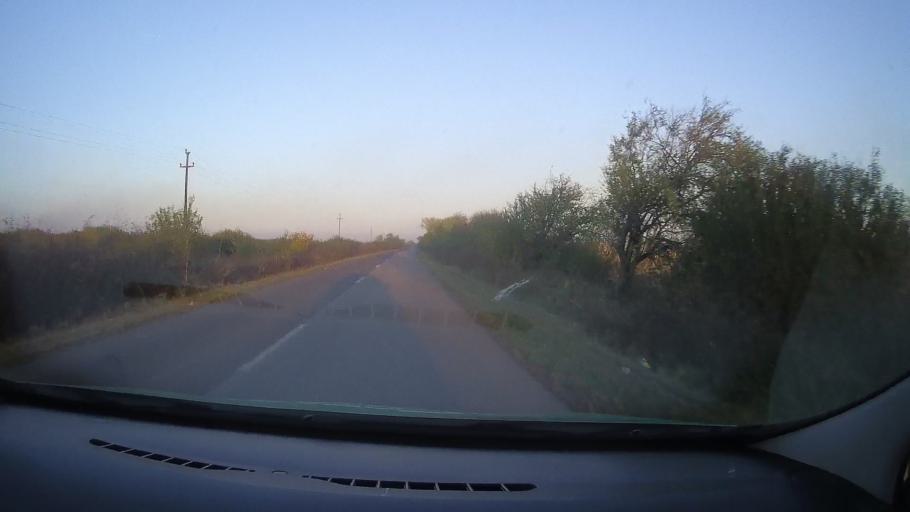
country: RO
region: Timis
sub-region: Comuna Manastiur
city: Manastiur
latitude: 45.8354
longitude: 22.0407
